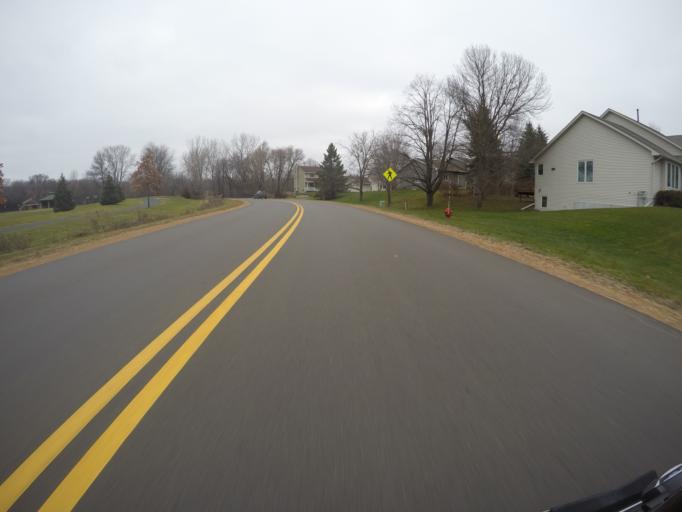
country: US
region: Minnesota
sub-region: Hennepin County
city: Eden Prairie
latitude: 44.8708
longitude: -93.4686
